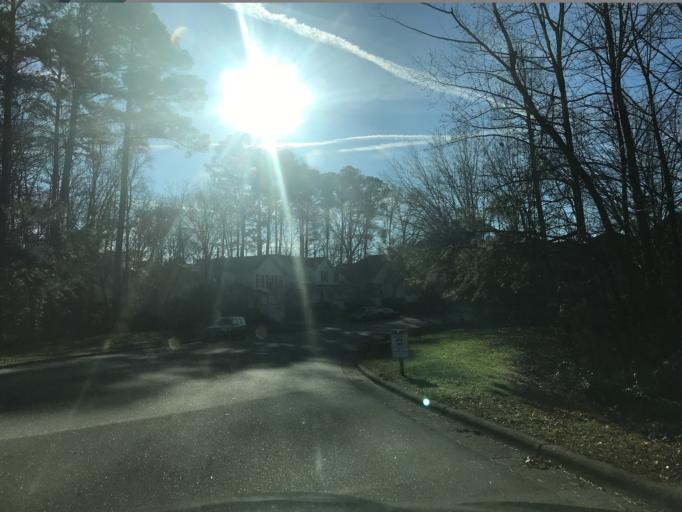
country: US
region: North Carolina
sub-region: Wake County
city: West Raleigh
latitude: 35.8880
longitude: -78.5957
